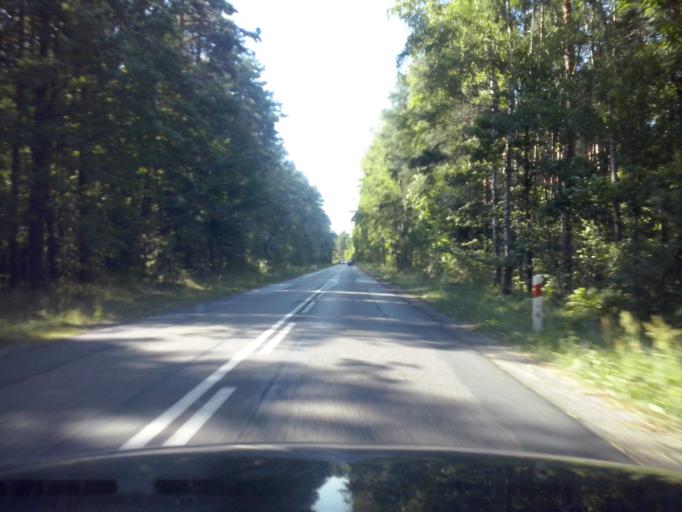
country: PL
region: Swietokrzyskie
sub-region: Powiat kielecki
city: Daleszyce
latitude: 50.8090
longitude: 20.7578
